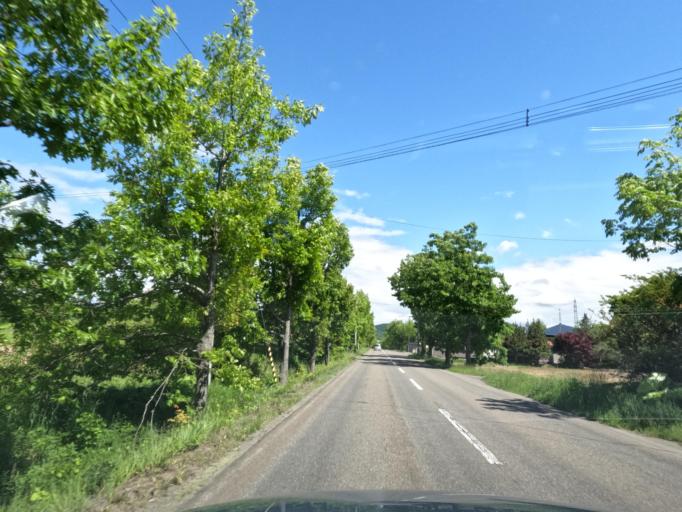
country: JP
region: Hokkaido
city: Kitahiroshima
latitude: 43.0208
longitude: 141.7104
